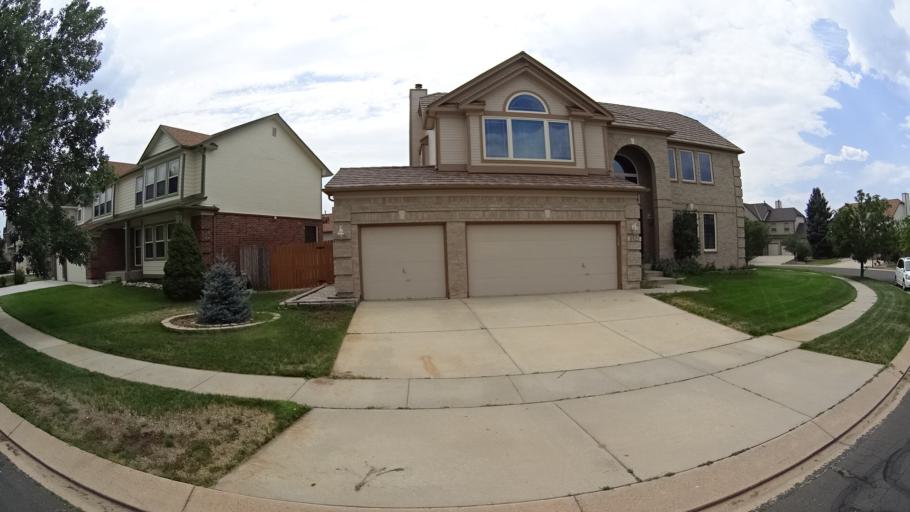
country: US
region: Colorado
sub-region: El Paso County
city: Air Force Academy
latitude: 38.9605
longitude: -104.7793
